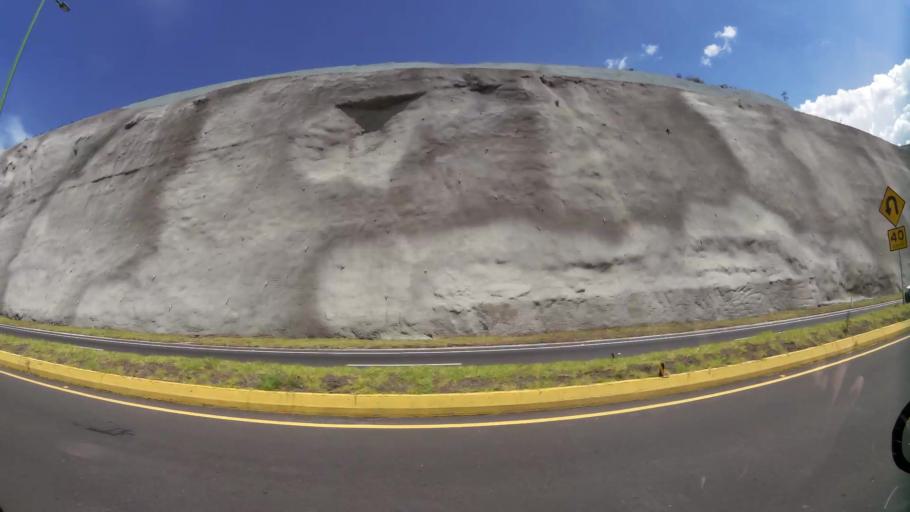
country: EC
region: Pichincha
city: Quito
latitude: -0.0997
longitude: -78.3832
